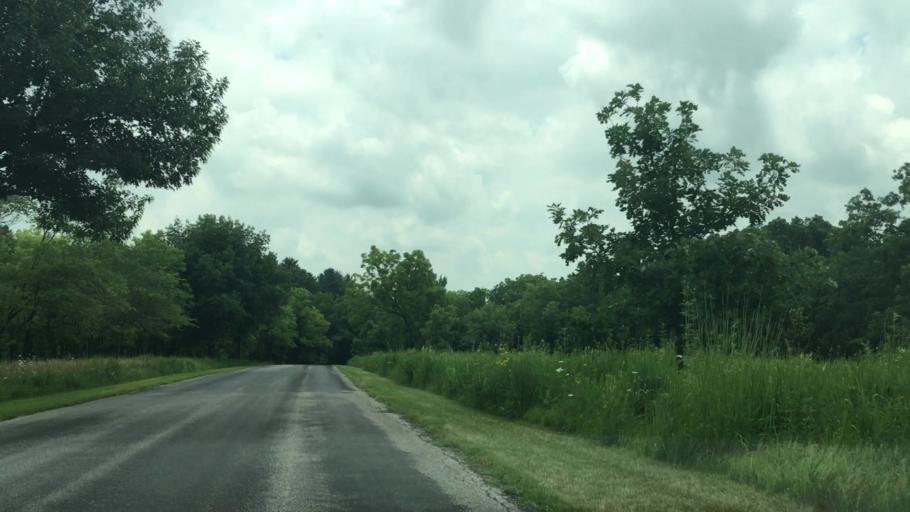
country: US
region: Iowa
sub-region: Johnson County
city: Tiffin
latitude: 41.7225
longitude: -91.7246
